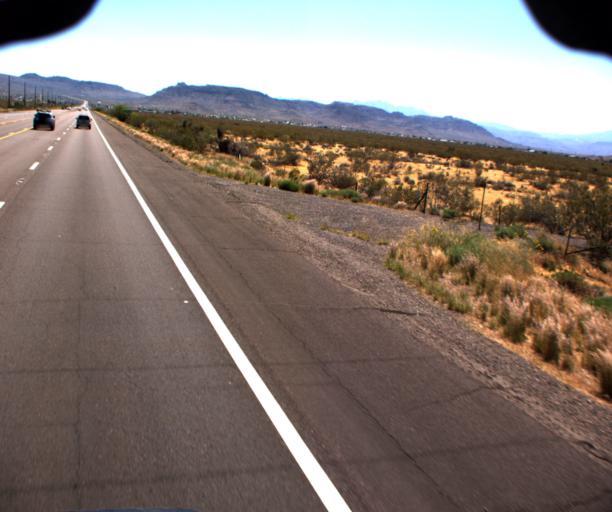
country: US
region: Arizona
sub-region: Mohave County
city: Golden Valley
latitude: 35.2213
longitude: -114.2031
